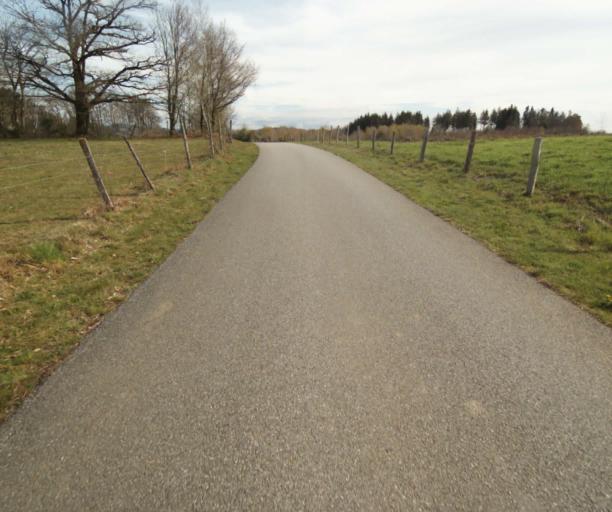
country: FR
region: Limousin
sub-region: Departement de la Correze
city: Correze
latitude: 45.3292
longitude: 1.8568
